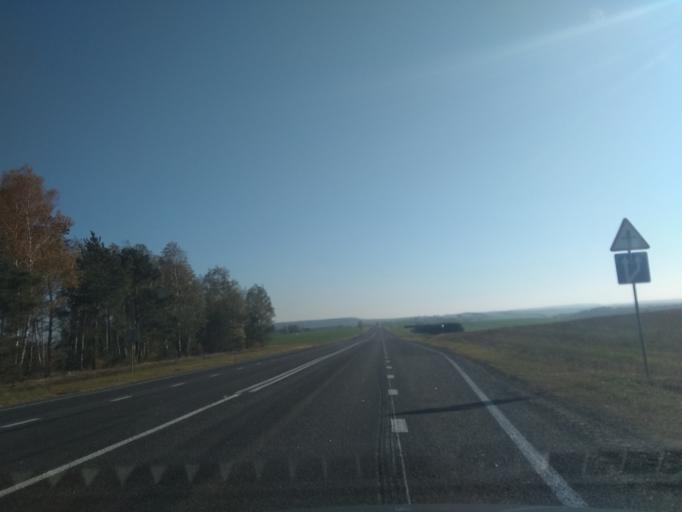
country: BY
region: Grodnenskaya
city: Zel'va
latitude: 53.1307
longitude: 25.0263
